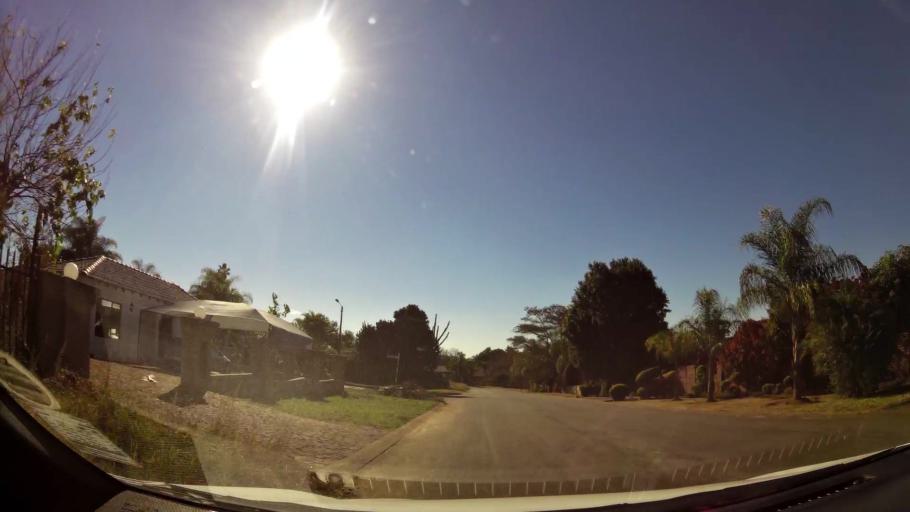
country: ZA
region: Limpopo
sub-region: Mopani District Municipality
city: Tzaneen
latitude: -23.8442
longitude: 30.1654
